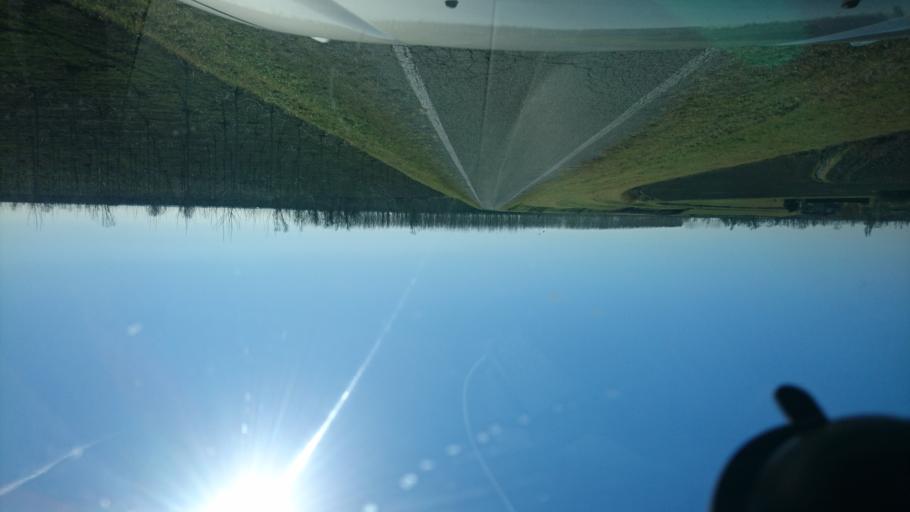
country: IT
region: Veneto
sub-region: Provincia di Rovigo
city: Ariano
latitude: 44.9366
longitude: 12.1298
